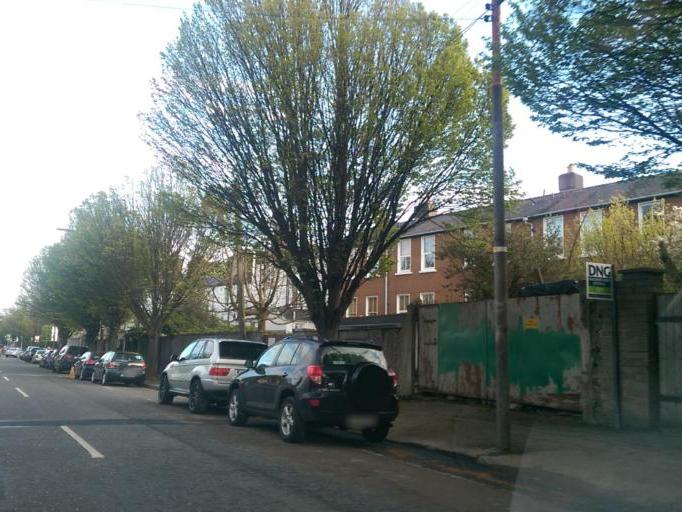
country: IE
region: Leinster
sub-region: Dublin City
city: Dublin
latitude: 53.3302
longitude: -6.2500
